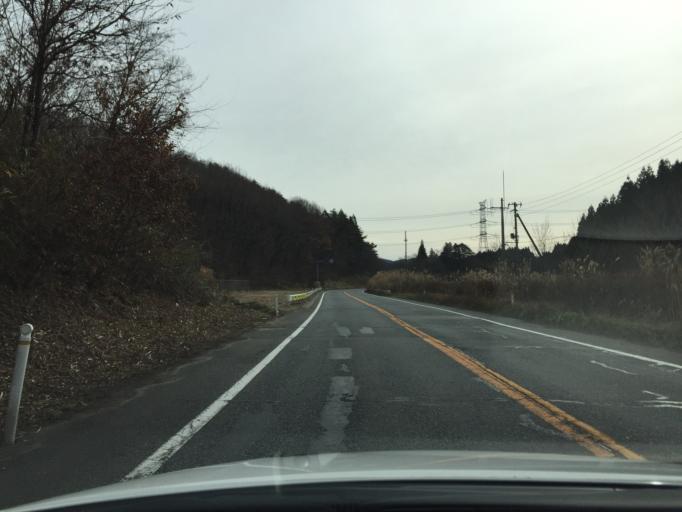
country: JP
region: Fukushima
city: Ishikawa
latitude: 37.2020
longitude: 140.6113
